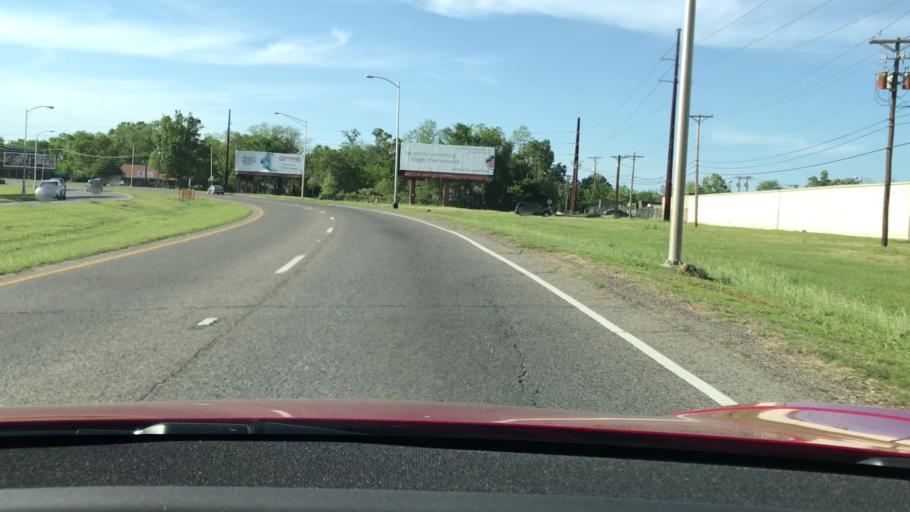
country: US
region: Louisiana
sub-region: Bossier Parish
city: Bossier City
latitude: 32.5016
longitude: -93.7248
